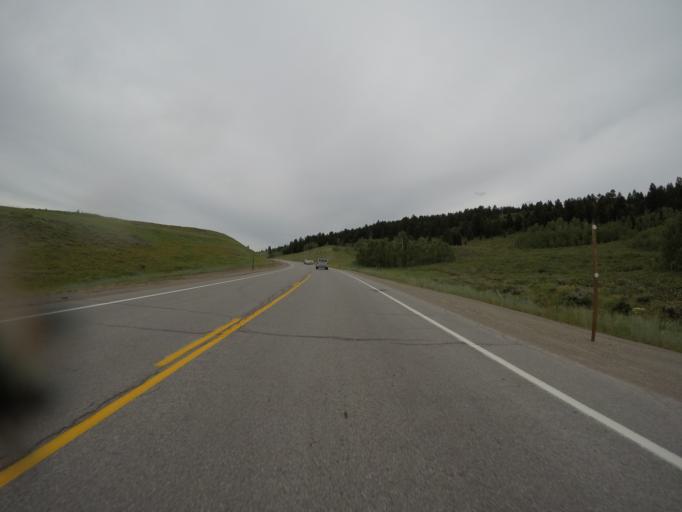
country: US
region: Wyoming
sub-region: Lincoln County
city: Afton
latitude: 42.4930
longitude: -110.9119
